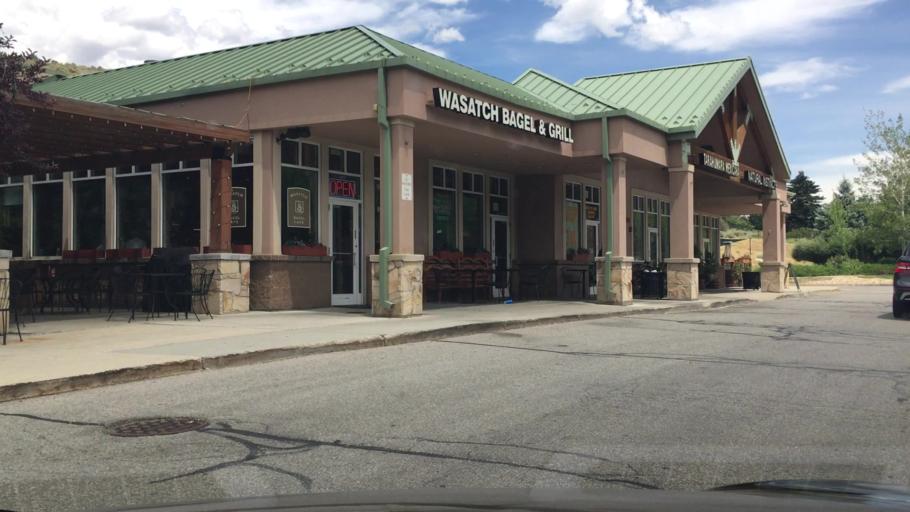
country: US
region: Utah
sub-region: Summit County
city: Park City
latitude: 40.6619
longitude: -111.5081
